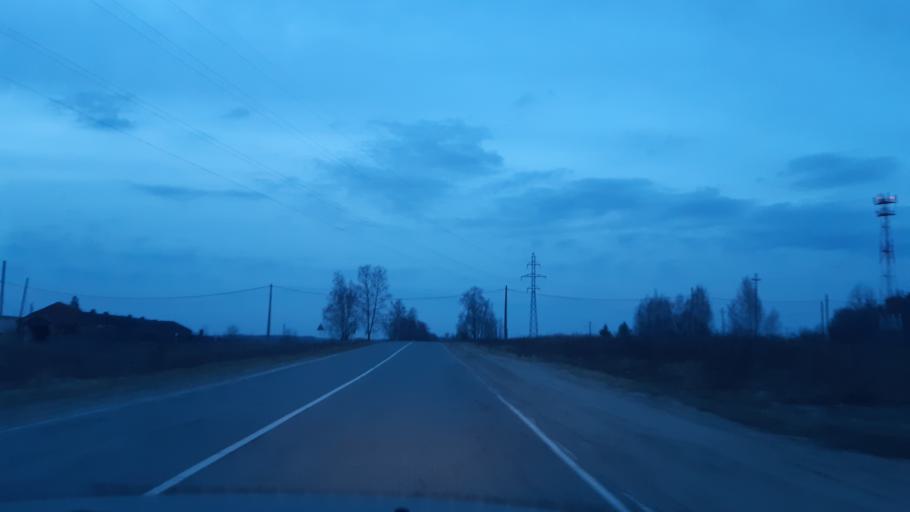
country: RU
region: Vladimir
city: Luknovo
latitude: 56.1988
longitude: 42.0339
